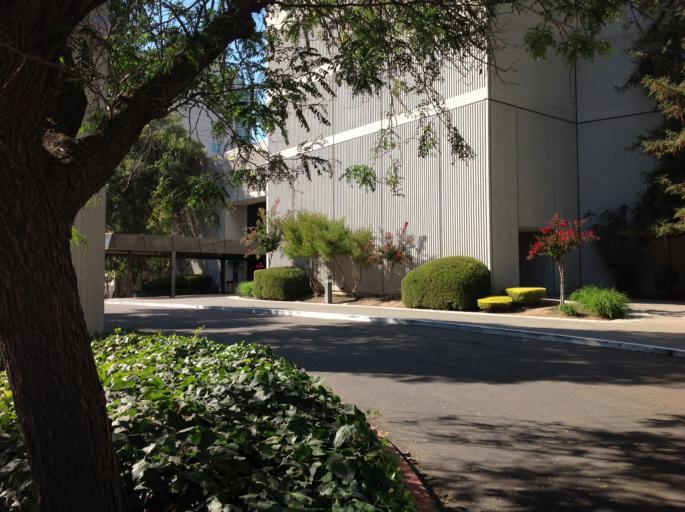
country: US
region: California
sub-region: Sacramento County
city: Sacramento
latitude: 38.5769
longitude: -121.4894
